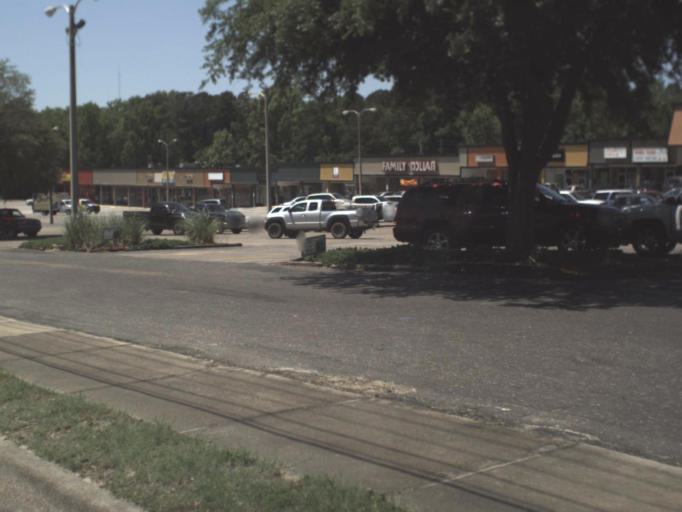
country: US
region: Florida
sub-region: Jefferson County
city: Monticello
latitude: 30.5353
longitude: -83.8703
